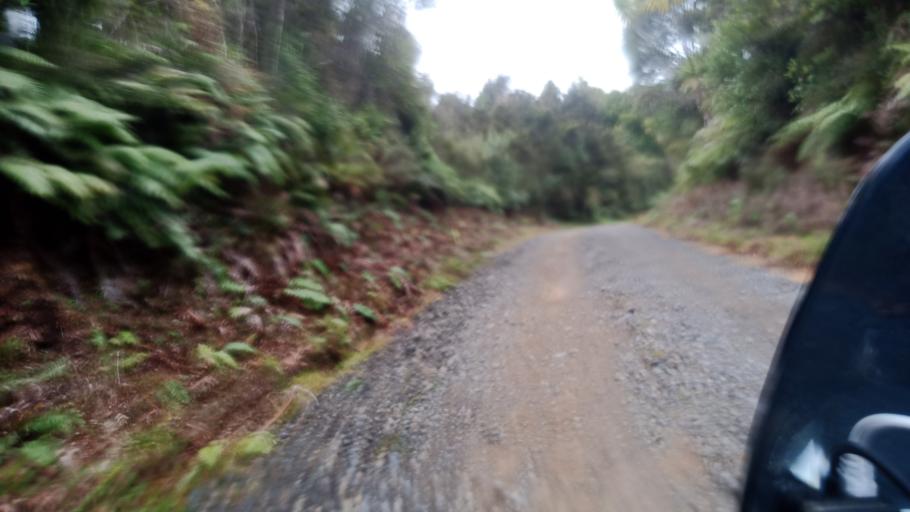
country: NZ
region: Bay of Plenty
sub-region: Whakatane District
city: Murupara
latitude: -38.6834
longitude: 176.6027
